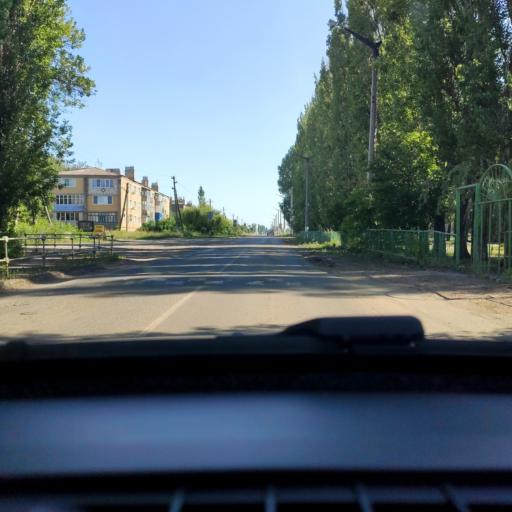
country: RU
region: Voronezj
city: Anna
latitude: 51.5075
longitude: 40.4358
